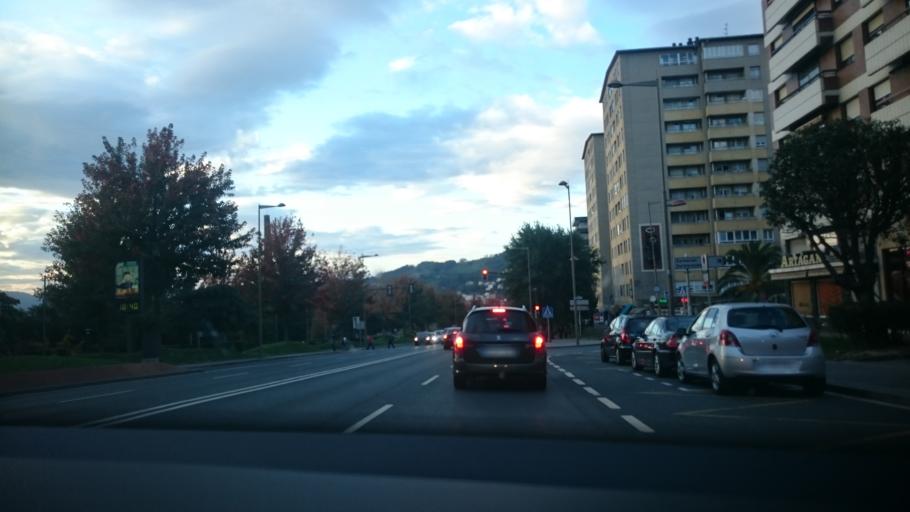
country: ES
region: Basque Country
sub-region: Bizkaia
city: Santutxu
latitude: 43.2615
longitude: -2.9154
